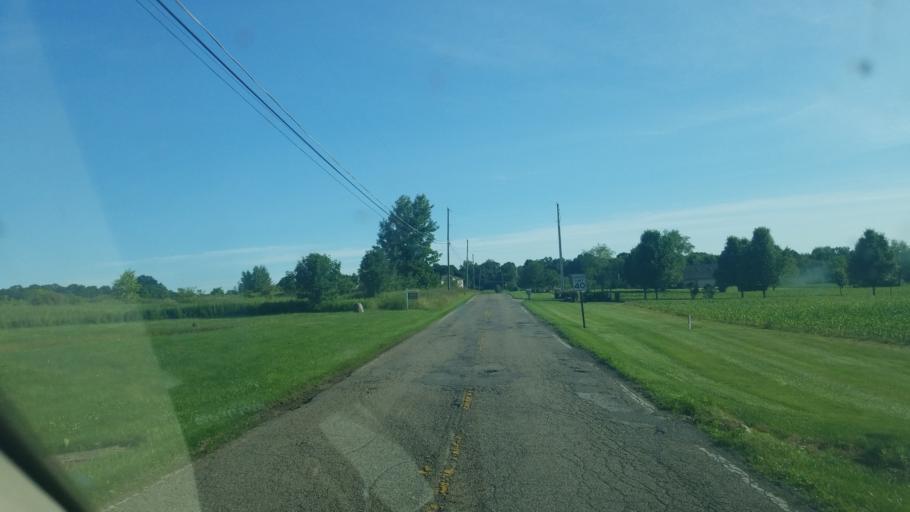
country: US
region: Ohio
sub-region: Columbiana County
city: Columbiana
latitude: 40.9139
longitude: -80.7034
